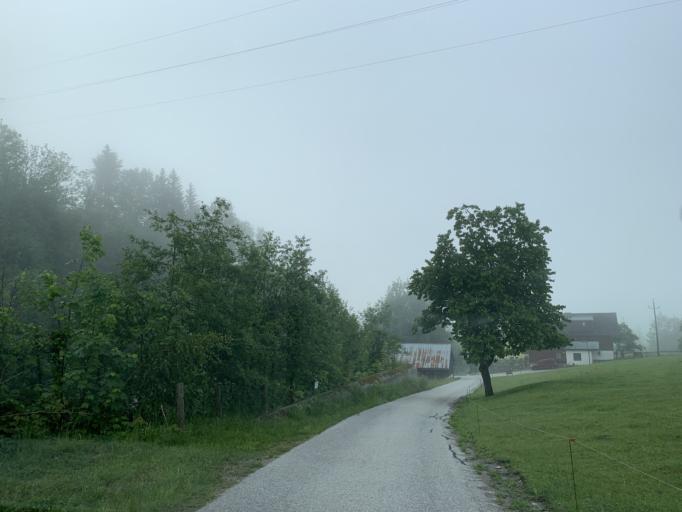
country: AT
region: Styria
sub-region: Politischer Bezirk Liezen
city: Schladming
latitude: 47.3913
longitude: 13.6201
